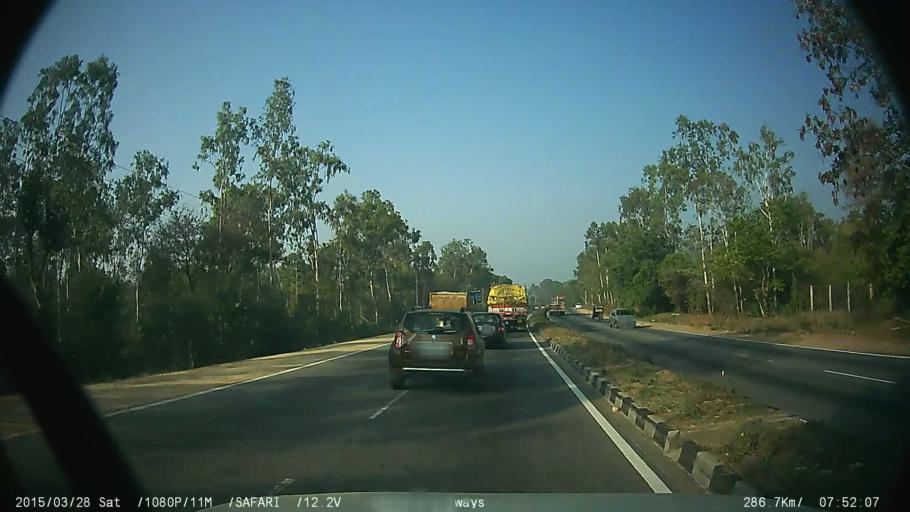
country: IN
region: Karnataka
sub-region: Mandya
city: Shrirangapattana
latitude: 12.4553
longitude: 76.7422
